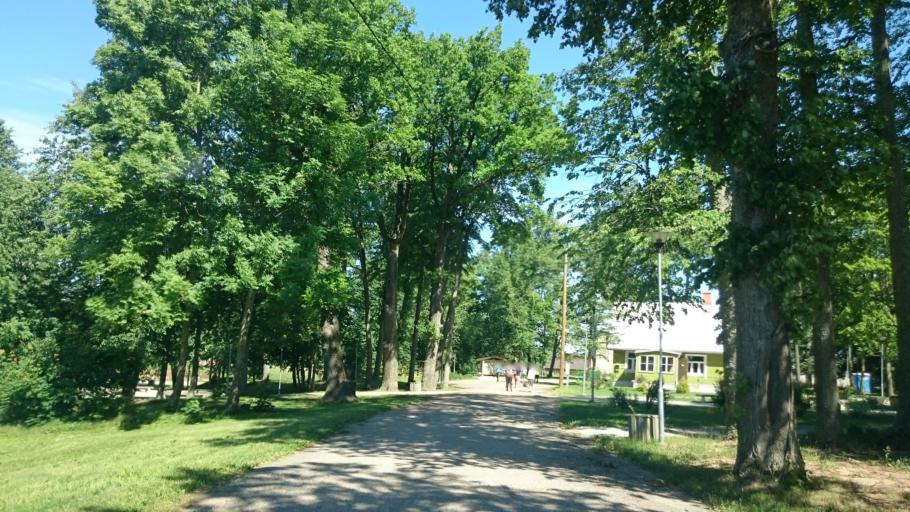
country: LV
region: Cibla
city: Cibla
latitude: 56.5930
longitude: 27.9901
